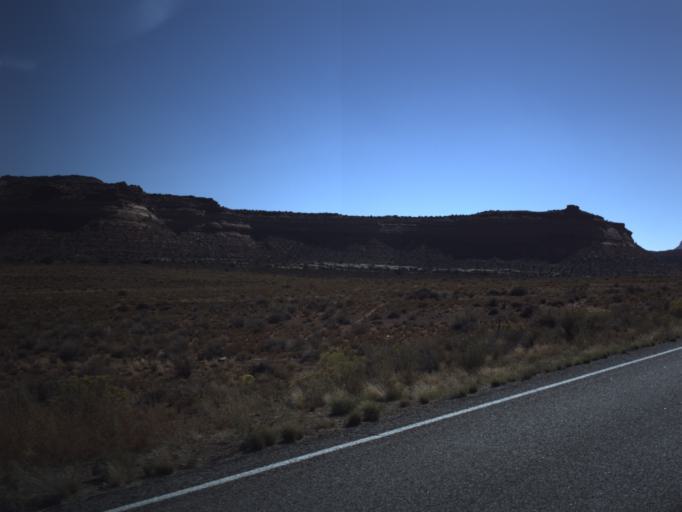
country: US
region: Utah
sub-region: San Juan County
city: Blanding
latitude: 37.7589
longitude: -110.2828
